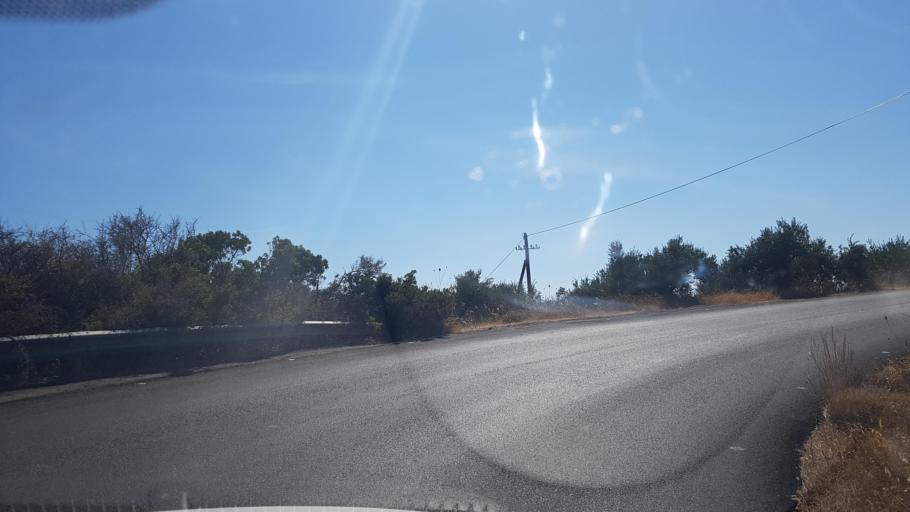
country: GR
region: Crete
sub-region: Nomos Chanias
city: Kissamos
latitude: 35.4977
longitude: 23.7217
